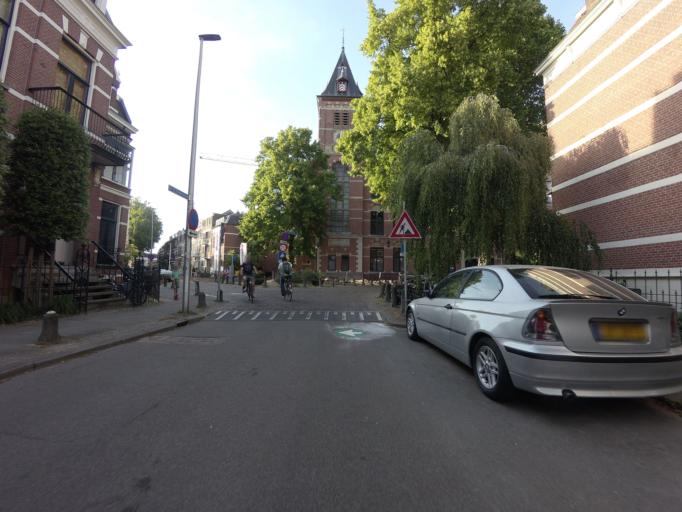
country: NL
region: Utrecht
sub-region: Gemeente Utrecht
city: Utrecht
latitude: 52.0978
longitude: 5.1387
